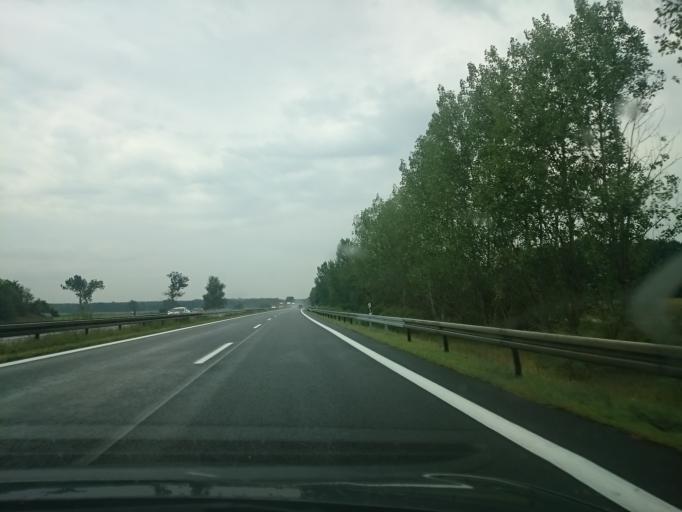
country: DE
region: Brandenburg
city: Brieselang
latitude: 52.6464
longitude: 12.9970
